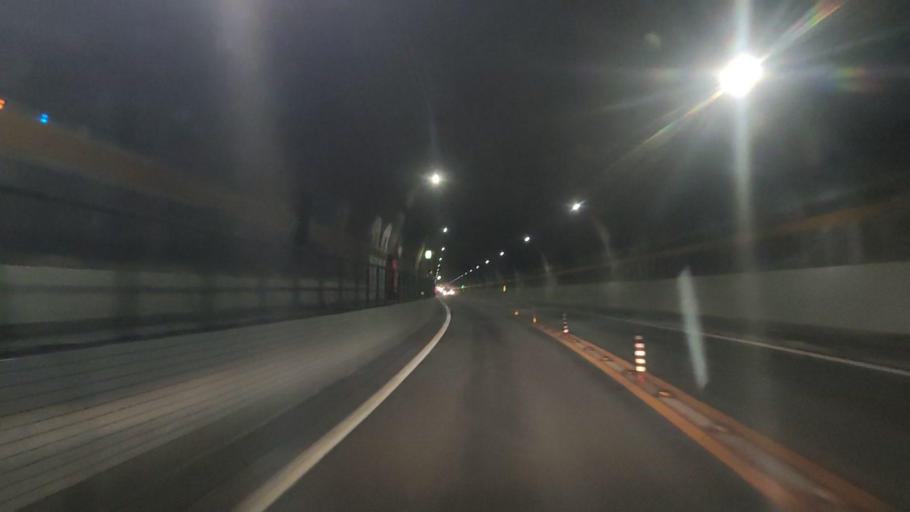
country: JP
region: Nagasaki
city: Obita
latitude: 32.7893
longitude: 129.8815
